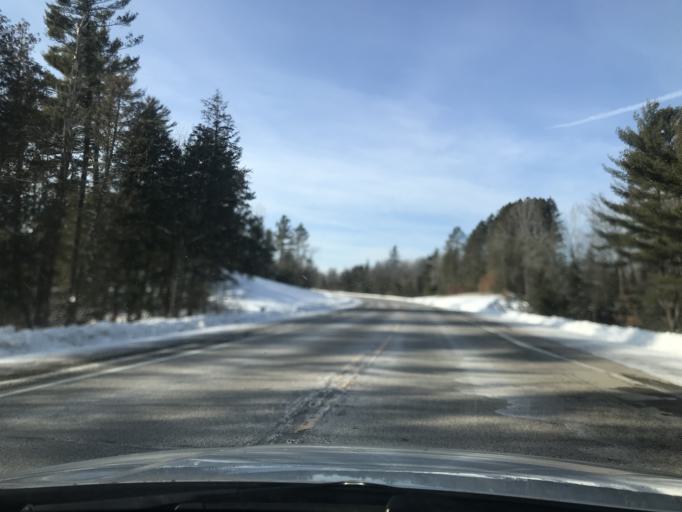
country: US
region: Wisconsin
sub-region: Oconto County
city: Gillett
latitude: 45.1275
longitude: -88.4049
